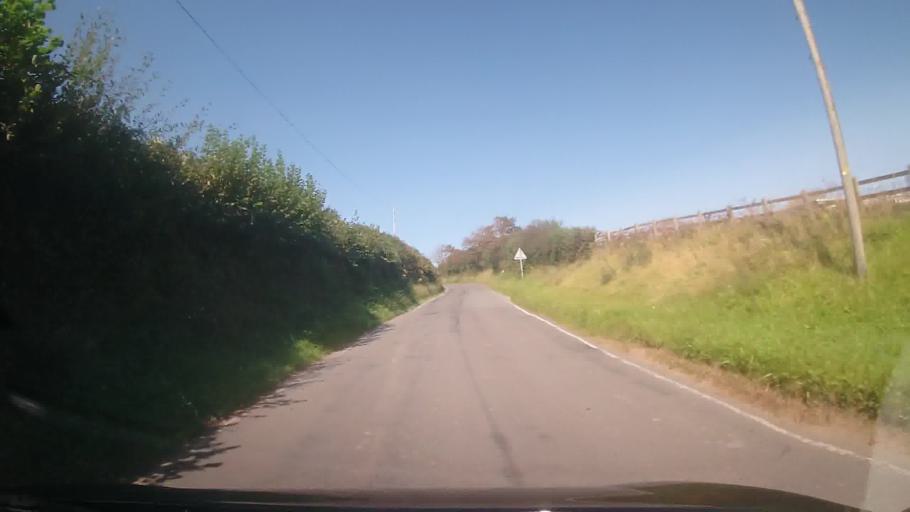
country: GB
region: Wales
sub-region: Pembrokeshire
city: Camrose
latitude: 51.8545
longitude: -5.0130
